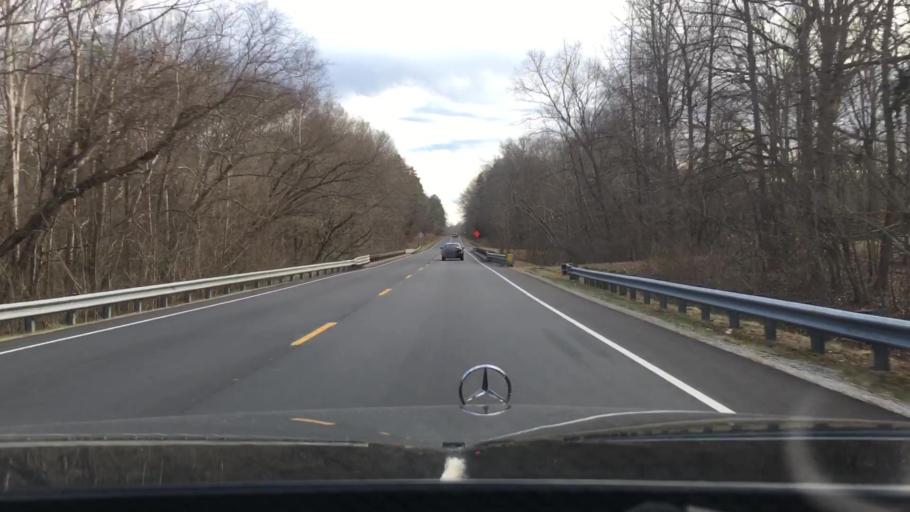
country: US
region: North Carolina
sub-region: Caswell County
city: Yanceyville
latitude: 36.4778
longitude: -79.3790
